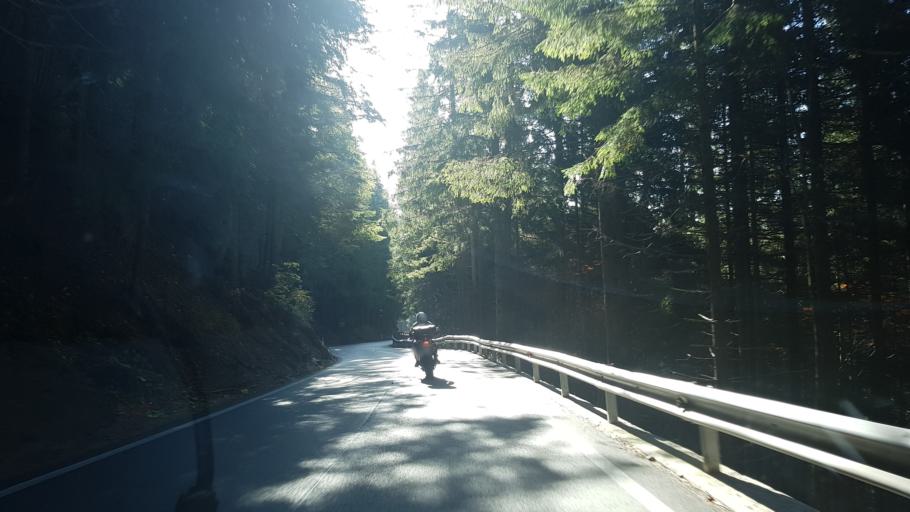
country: IT
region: Veneto
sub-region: Provincia di Belluno
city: Candide
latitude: 46.6418
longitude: 12.4560
